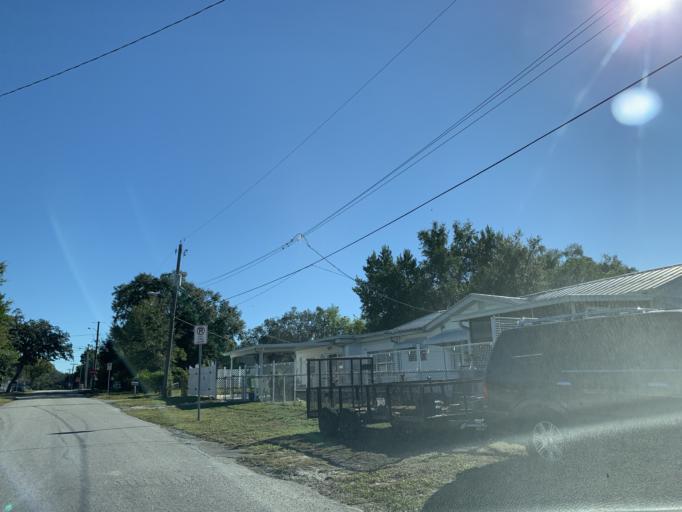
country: US
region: Florida
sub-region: Hillsborough County
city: Temple Terrace
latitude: 28.0253
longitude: -82.4181
